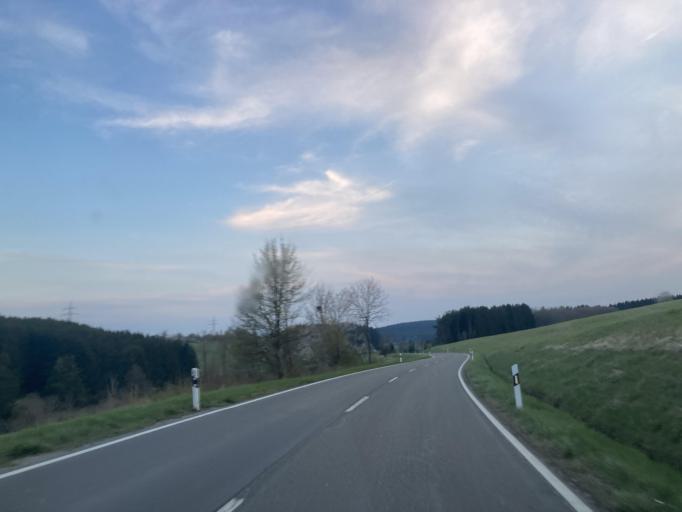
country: DE
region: Baden-Wuerttemberg
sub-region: Tuebingen Region
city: Weilen unter den Rinnen
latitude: 48.1811
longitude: 8.7327
